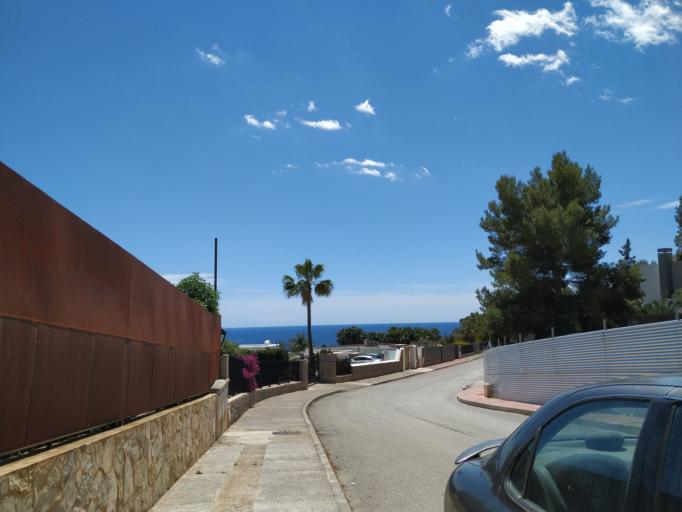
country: ES
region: Balearic Islands
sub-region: Illes Balears
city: Ibiza
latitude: 38.9189
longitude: 1.4730
